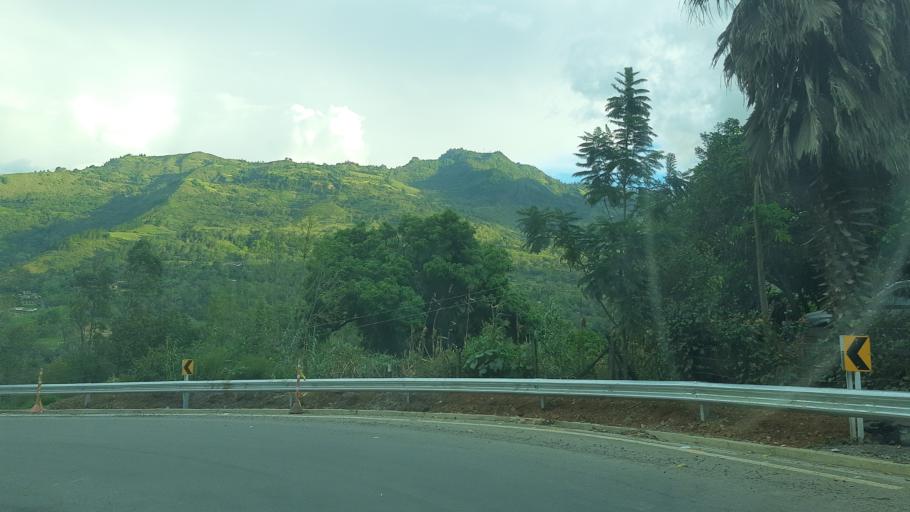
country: CO
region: Boyaca
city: Somondoco
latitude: 5.0091
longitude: -73.4337
